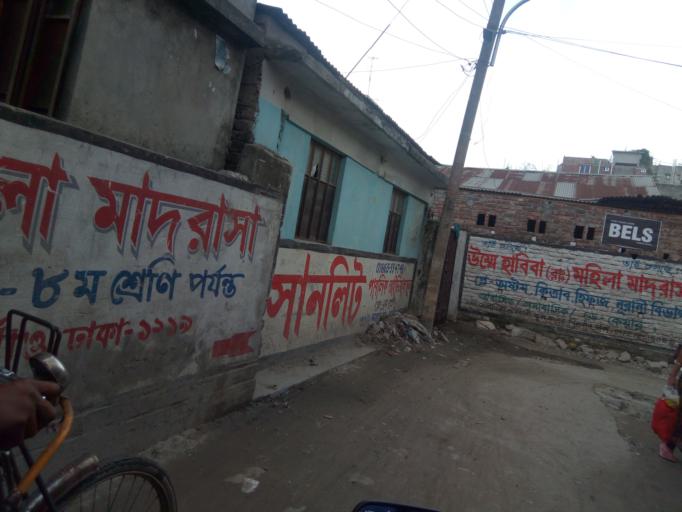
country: BD
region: Dhaka
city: Paltan
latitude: 23.7531
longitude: 90.4340
